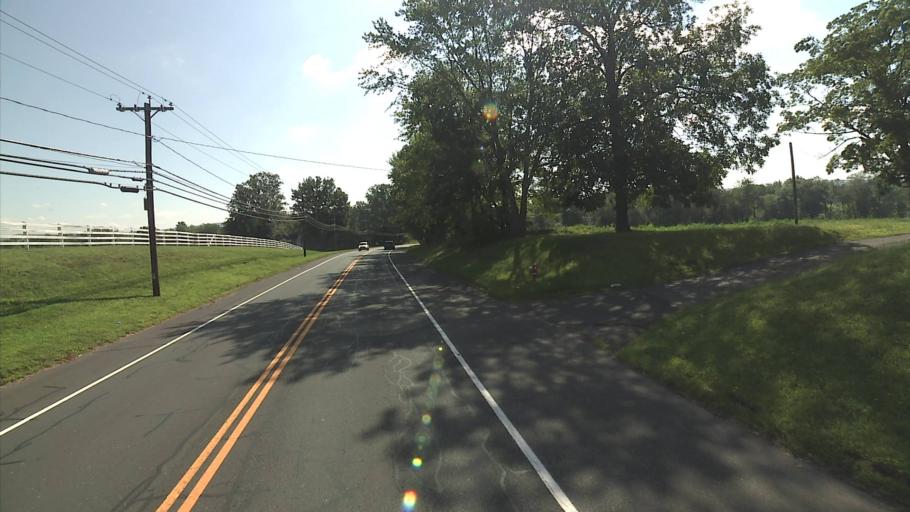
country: US
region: Connecticut
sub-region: Tolland County
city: Somers
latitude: 41.9871
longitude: -72.4765
